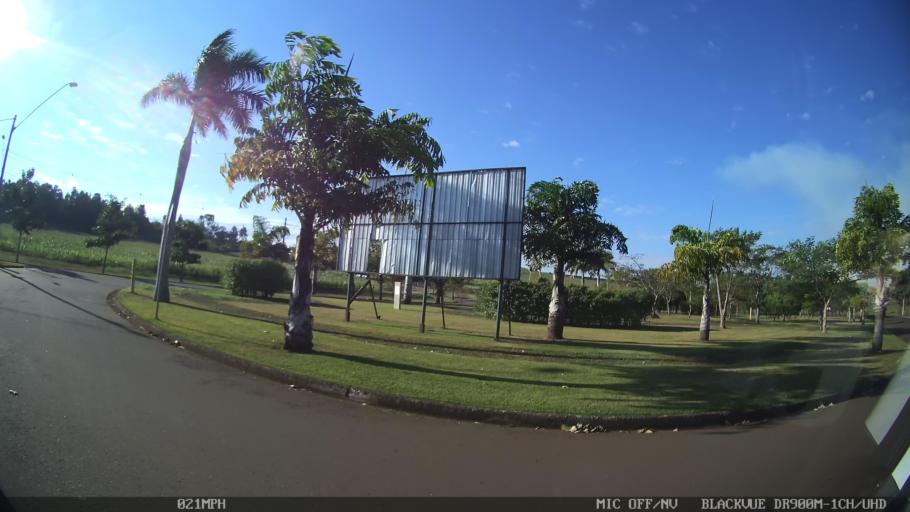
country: BR
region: Sao Paulo
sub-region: Piracicaba
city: Piracicaba
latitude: -22.6953
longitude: -47.6160
